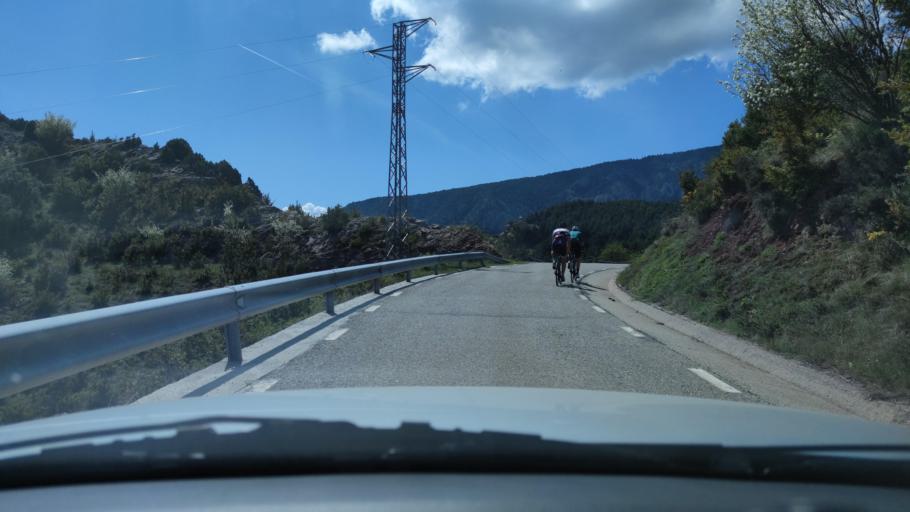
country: ES
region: Catalonia
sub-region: Provincia de Lleida
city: Coll de Nargo
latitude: 42.3045
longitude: 1.2833
